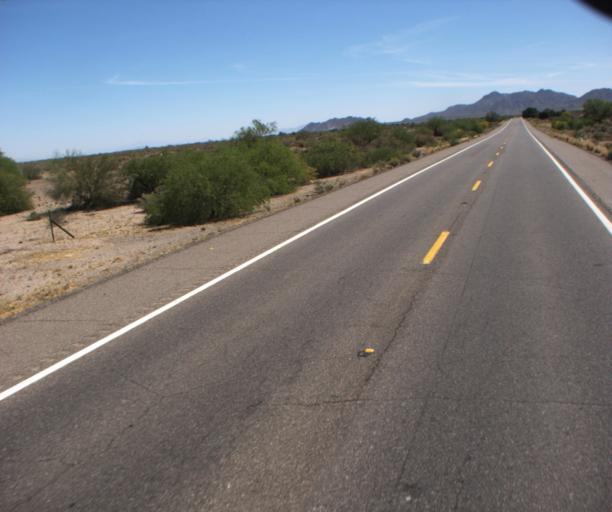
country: US
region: Arizona
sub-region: Pinal County
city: Sacaton
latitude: 33.0948
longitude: -111.7099
